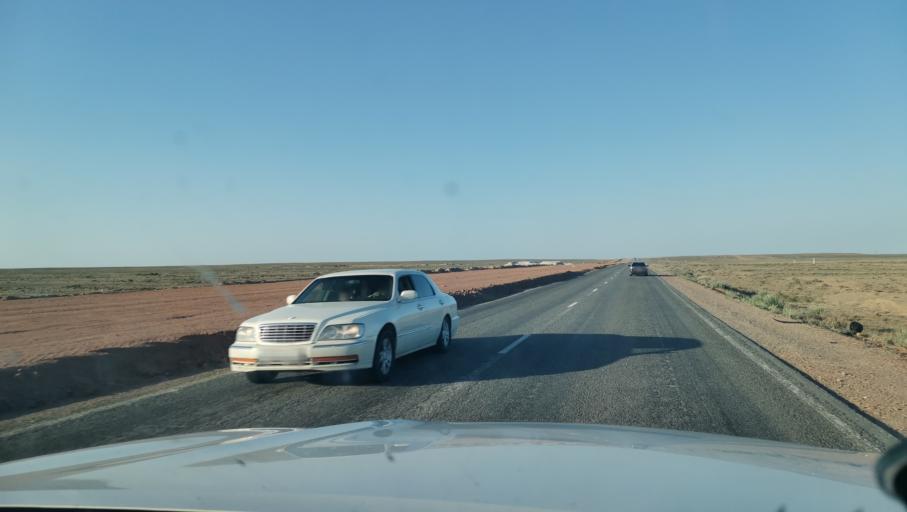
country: KZ
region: Qaraghandy
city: Saryshaghan
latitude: 46.4752
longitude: 74.0413
